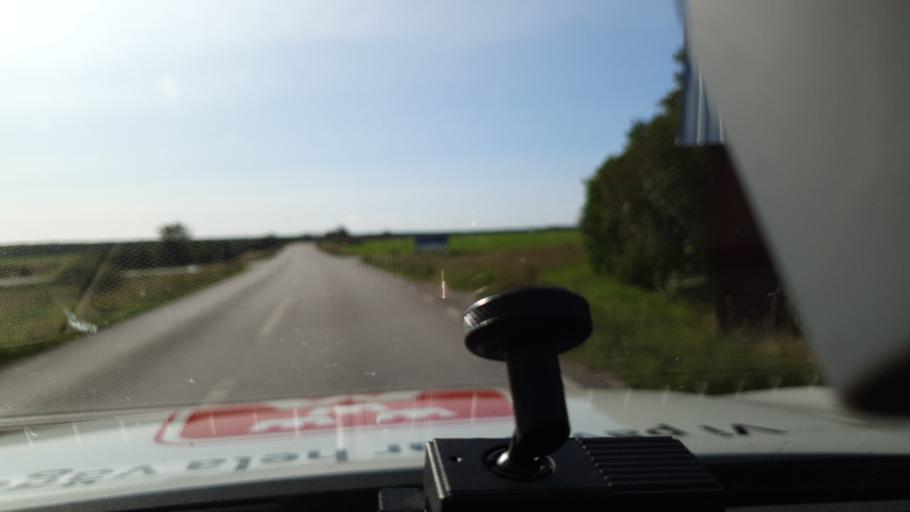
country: SE
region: Gotland
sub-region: Gotland
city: Hemse
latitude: 57.1439
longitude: 18.2850
